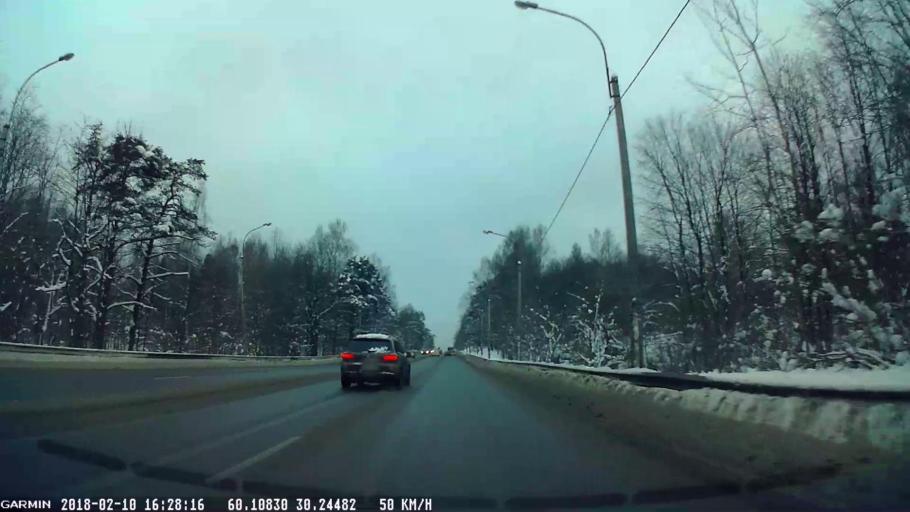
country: RU
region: St.-Petersburg
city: Levashovo
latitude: 60.1086
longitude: 30.2446
